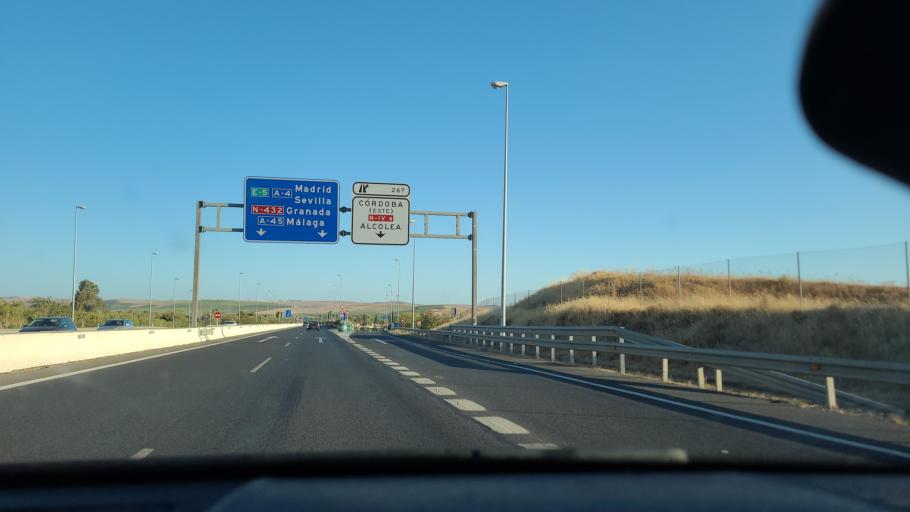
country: ES
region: Andalusia
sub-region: Province of Cordoba
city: Cordoba
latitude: 37.8993
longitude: -4.7486
